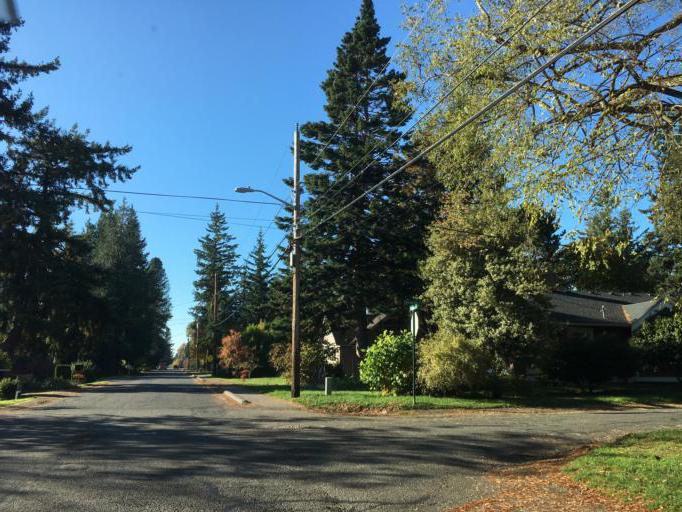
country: US
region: Washington
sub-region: Whatcom County
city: Bellingham
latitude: 48.7739
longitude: -122.5029
